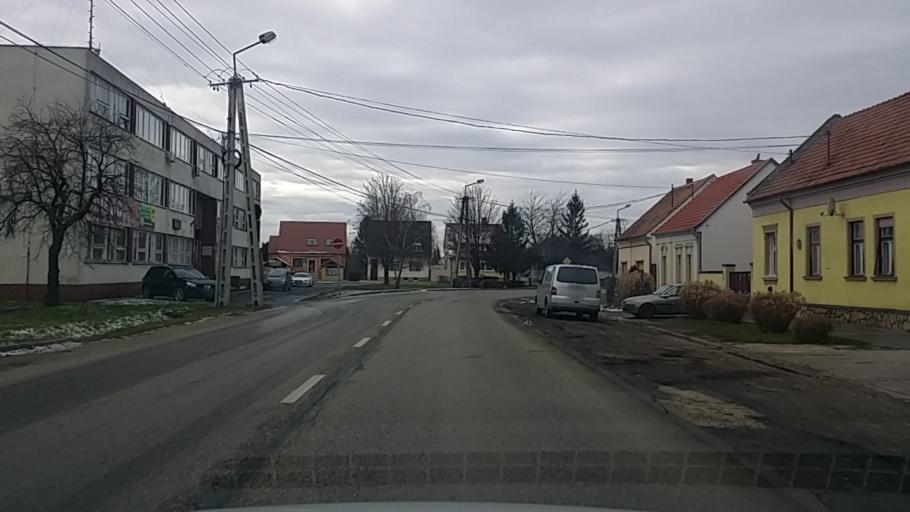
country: HU
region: Veszprem
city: Papa
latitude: 47.3217
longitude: 17.4736
